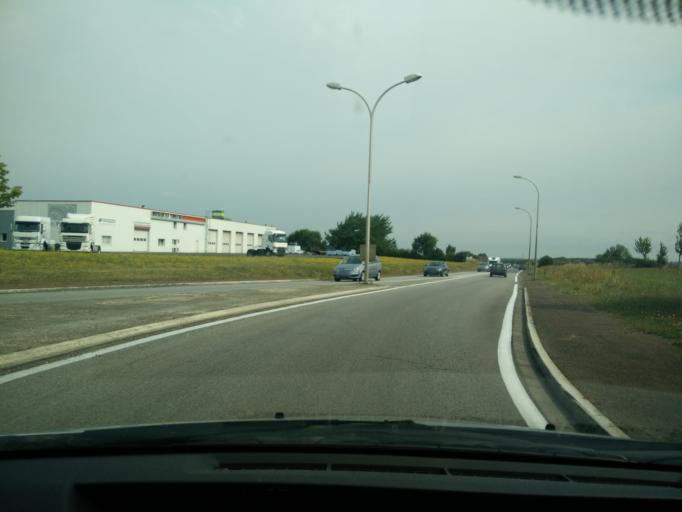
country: FR
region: Poitou-Charentes
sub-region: Departement des Deux-Sevres
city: Sainte-Verge
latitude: 46.9904
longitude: -0.1962
